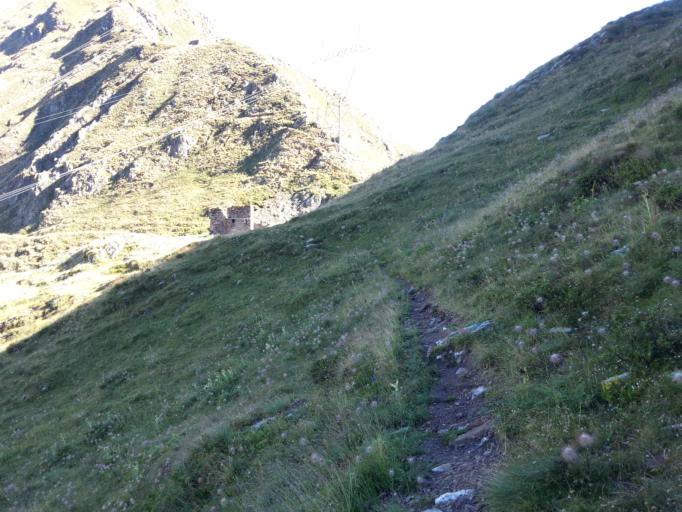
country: IT
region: Lombardy
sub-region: Provincia di Sondrio
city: Gerola Alta
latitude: 46.0301
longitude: 9.5221
